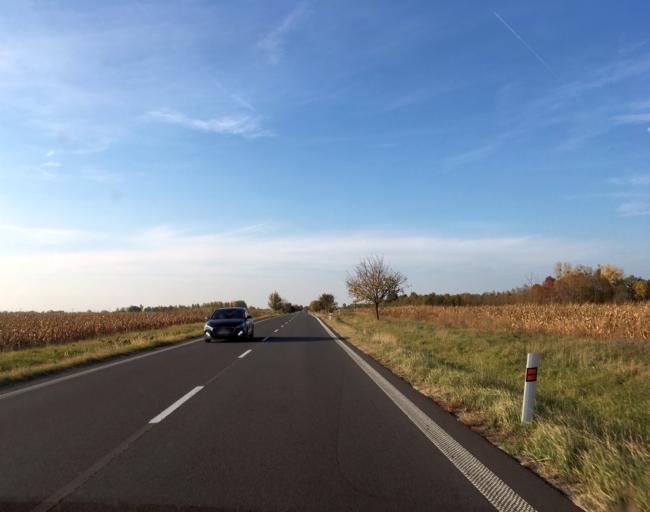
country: SK
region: Nitriansky
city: Surany
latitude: 48.0698
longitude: 18.0922
